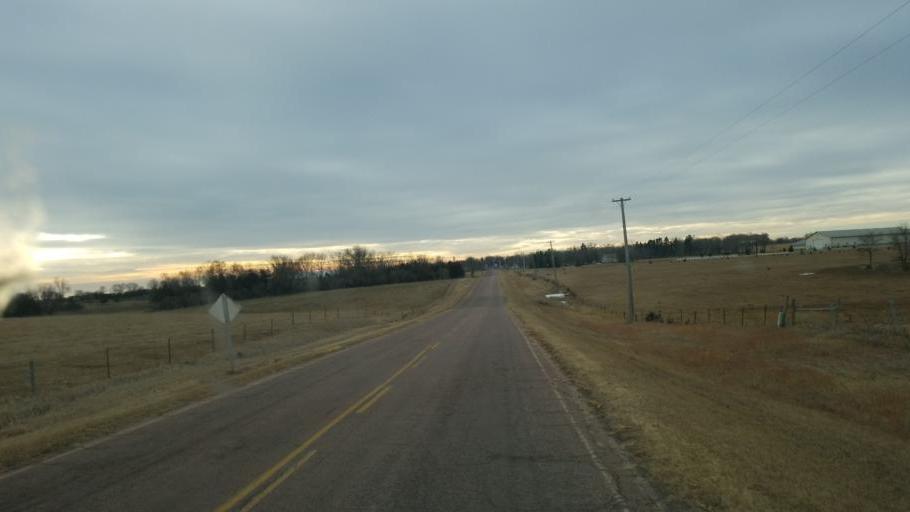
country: US
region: South Dakota
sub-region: Hutchinson County
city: Parkston
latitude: 43.2400
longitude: -97.9661
